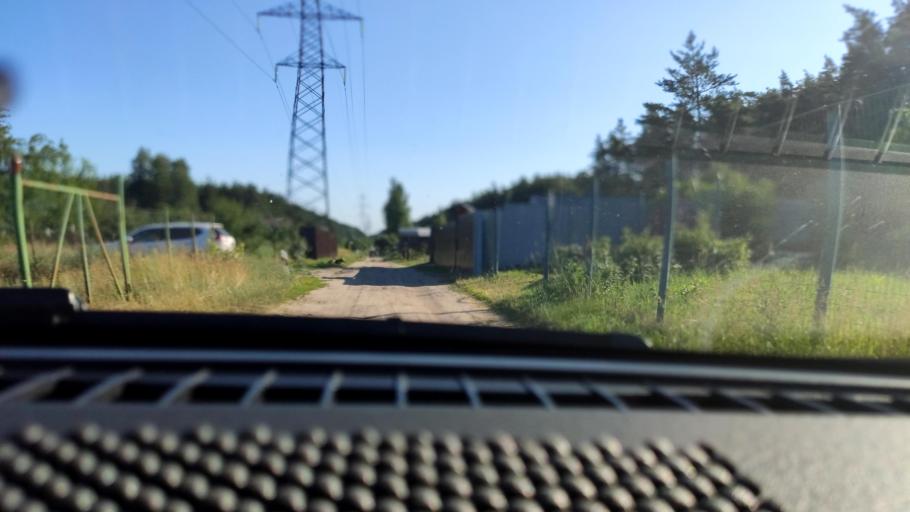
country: RU
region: Voronezj
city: Volya
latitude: 51.7431
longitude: 39.4606
